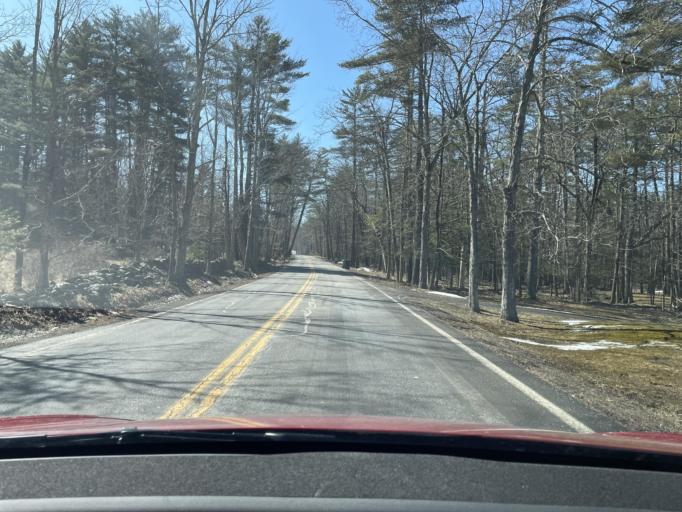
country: US
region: New York
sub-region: Ulster County
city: Woodstock
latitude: 42.0192
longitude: -74.1340
